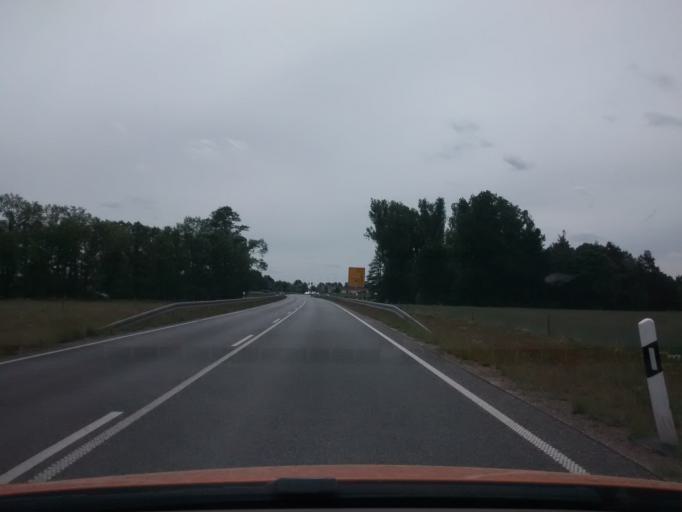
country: DE
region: Brandenburg
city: Juterbog
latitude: 52.0365
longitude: 13.1062
